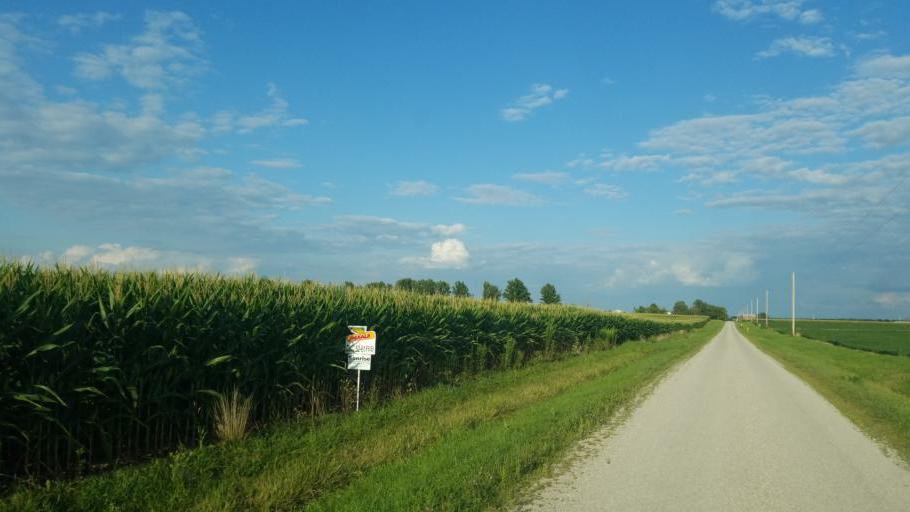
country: US
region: Ohio
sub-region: Sandusky County
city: Mount Carmel
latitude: 41.1101
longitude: -82.9093
